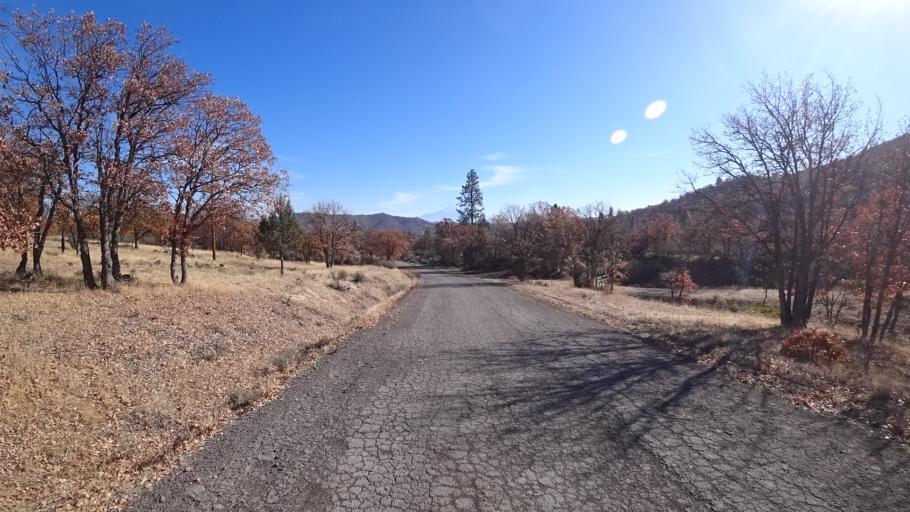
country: US
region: California
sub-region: Siskiyou County
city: Yreka
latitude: 41.7717
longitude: -122.6419
